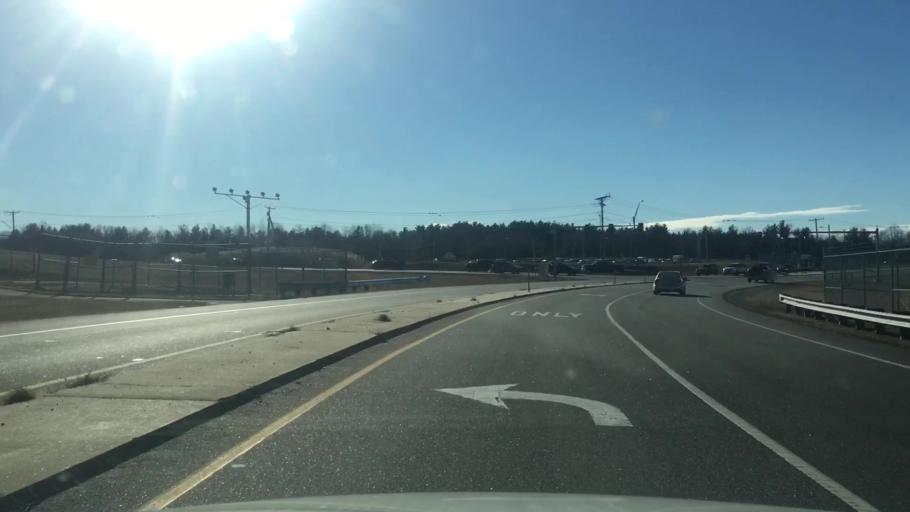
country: US
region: New Hampshire
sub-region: Rockingham County
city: Londonderry
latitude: 42.9152
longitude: -71.4235
